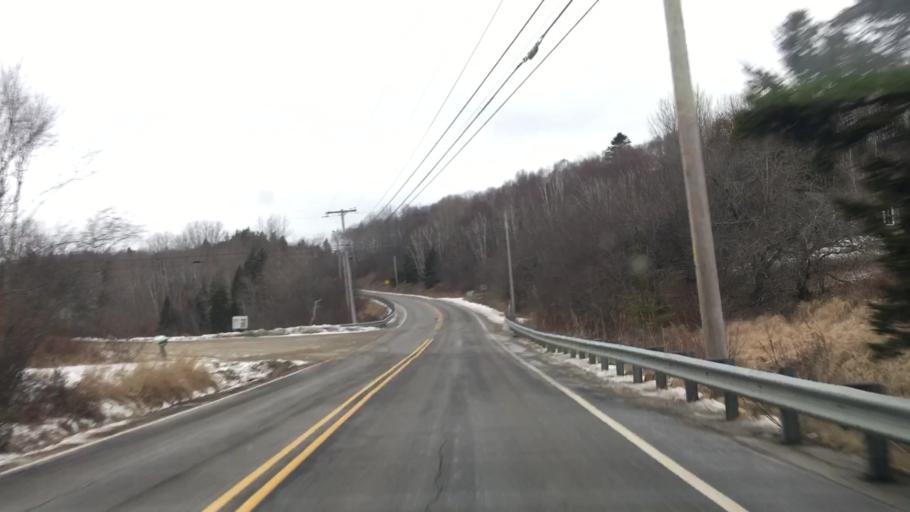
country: US
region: Maine
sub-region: Washington County
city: Machiasport
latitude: 44.7131
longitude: -67.3744
